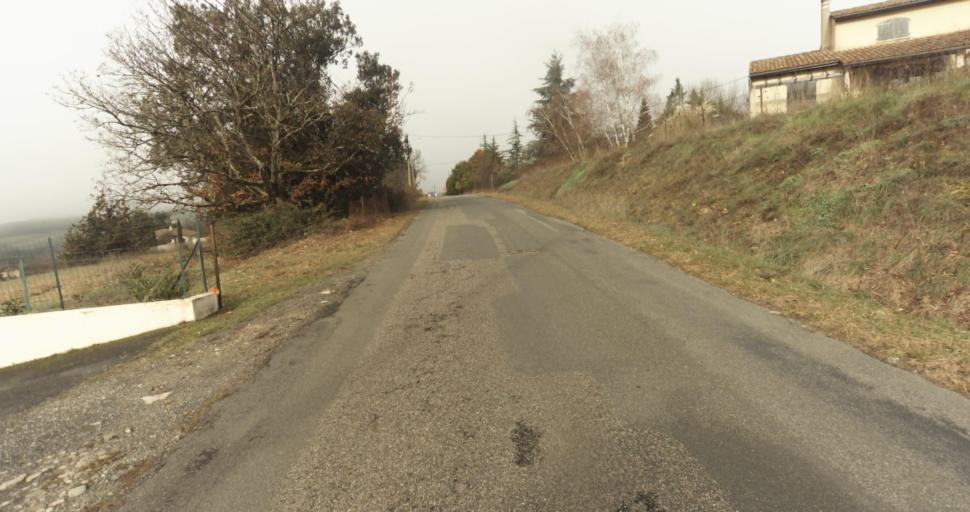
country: FR
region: Midi-Pyrenees
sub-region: Departement du Lot
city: Figeac
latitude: 44.6195
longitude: 2.0245
